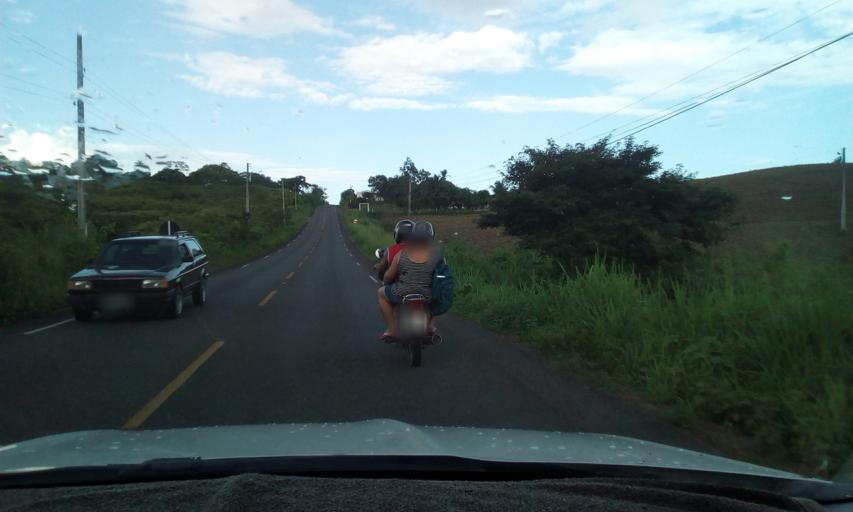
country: BR
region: Paraiba
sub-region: Guarabira
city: Guarabira
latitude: -6.8581
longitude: -35.4367
